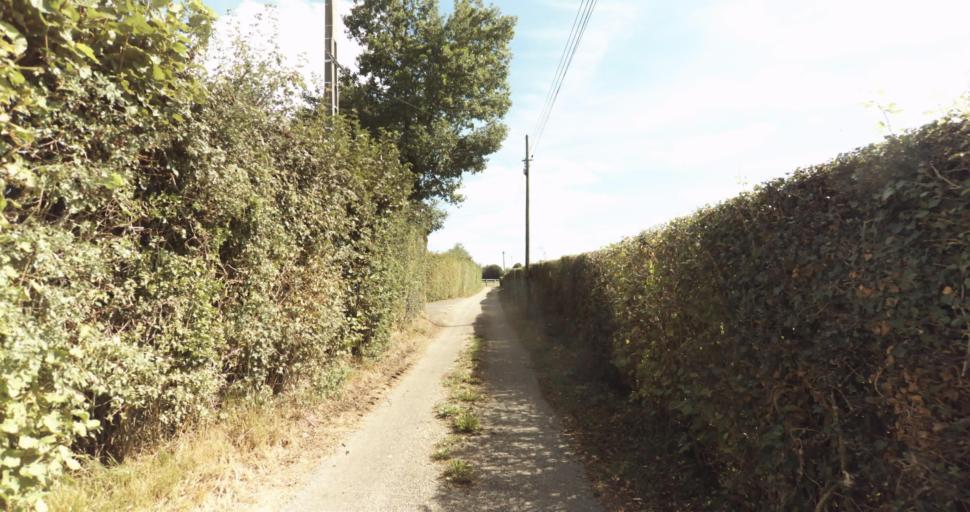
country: FR
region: Lower Normandy
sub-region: Departement de l'Orne
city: Vimoutiers
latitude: 48.9266
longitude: 0.2352
